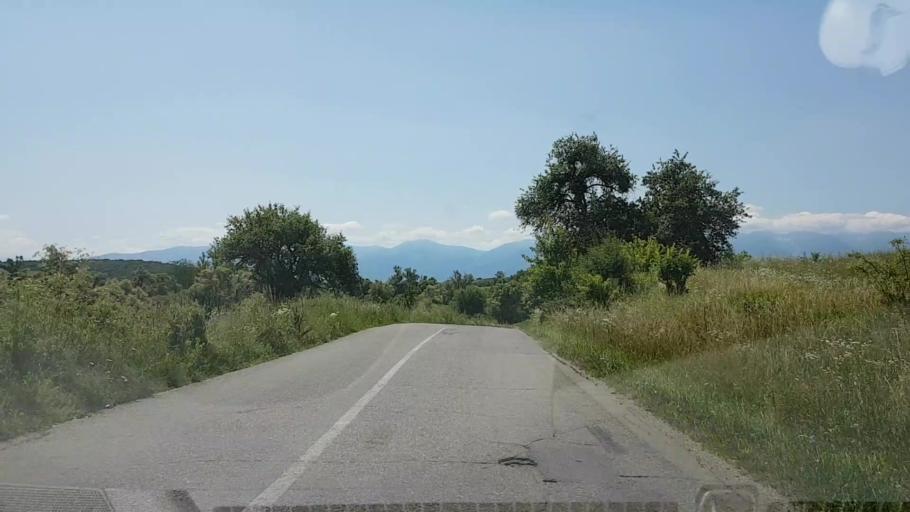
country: RO
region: Brasov
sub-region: Comuna Voila
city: Voila
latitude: 45.8643
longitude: 24.8254
